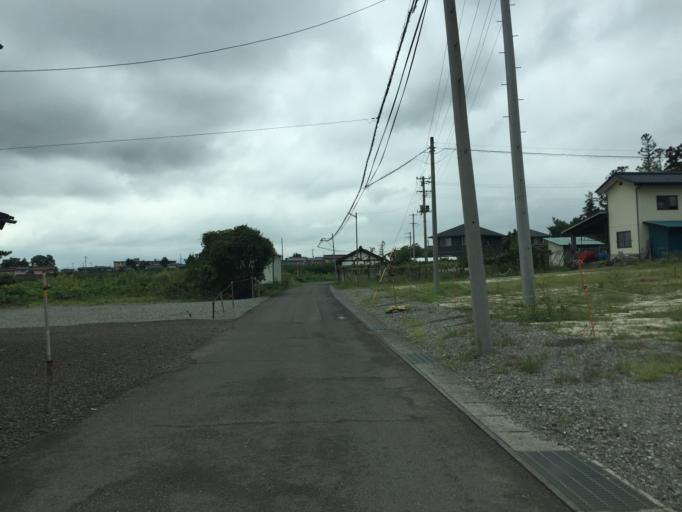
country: JP
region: Fukushima
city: Fukushima-shi
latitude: 37.8054
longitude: 140.4030
